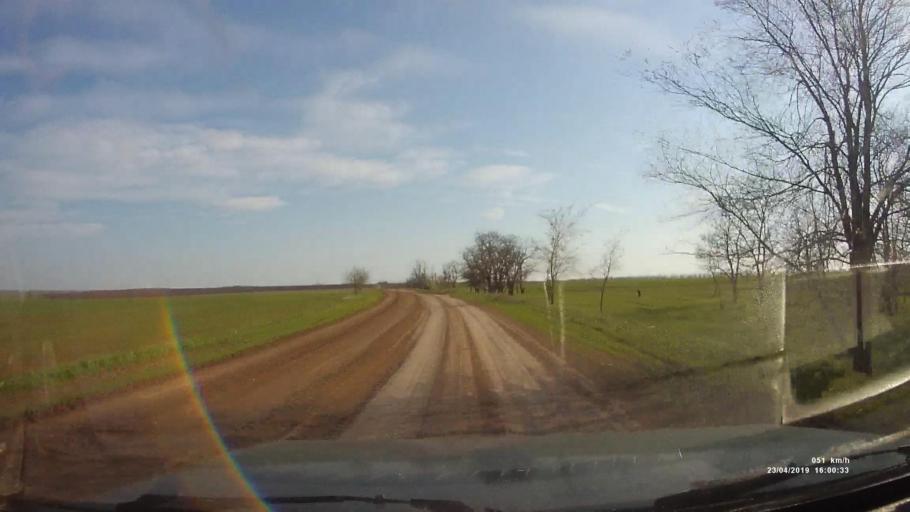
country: RU
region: Rostov
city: Remontnoye
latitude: 46.5087
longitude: 43.1072
